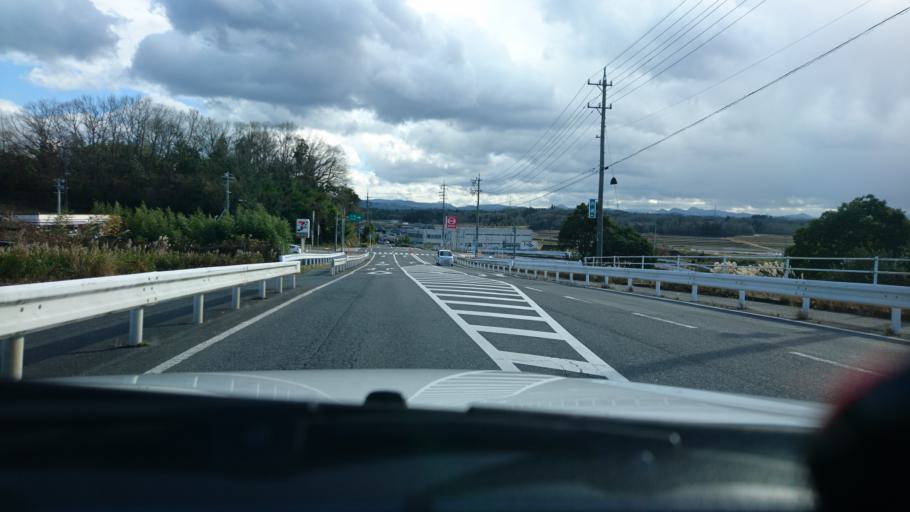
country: JP
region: Mie
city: Ueno-ebisumachi
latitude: 34.7542
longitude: 136.1477
